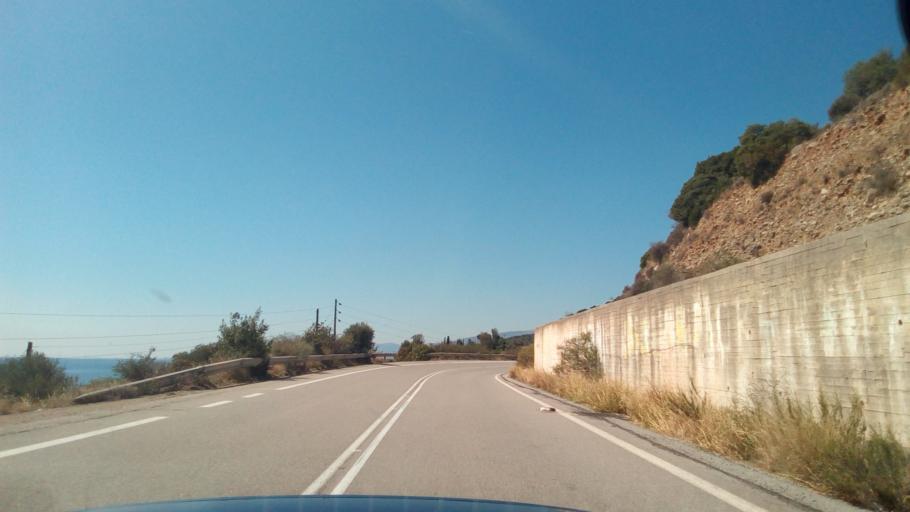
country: GR
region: West Greece
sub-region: Nomos Achaias
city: Kamarai
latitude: 38.4001
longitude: 21.9980
